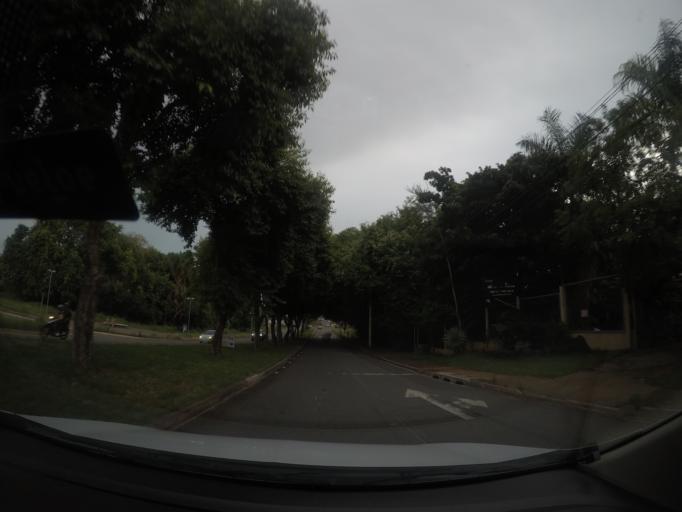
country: BR
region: Goias
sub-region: Goiania
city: Goiania
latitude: -16.7378
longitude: -49.3120
